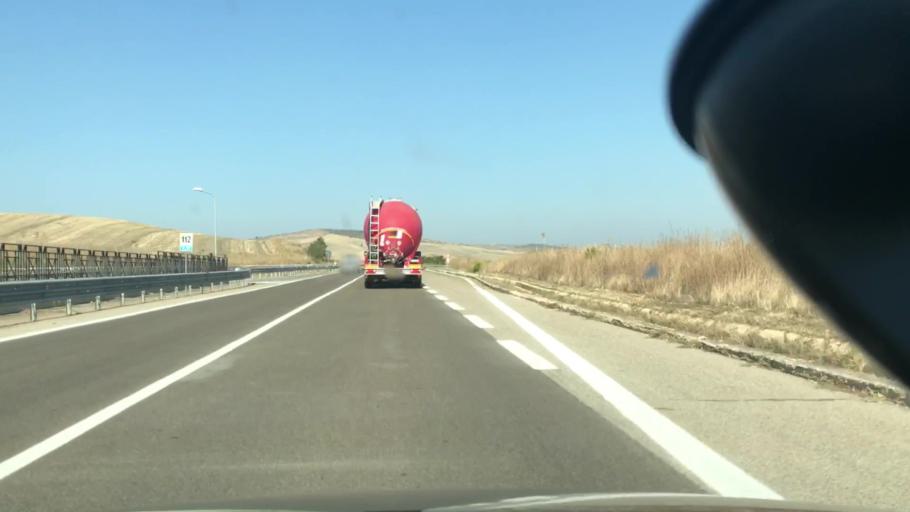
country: IT
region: Basilicate
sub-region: Provincia di Matera
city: Irsina
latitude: 40.7859
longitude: 16.2964
